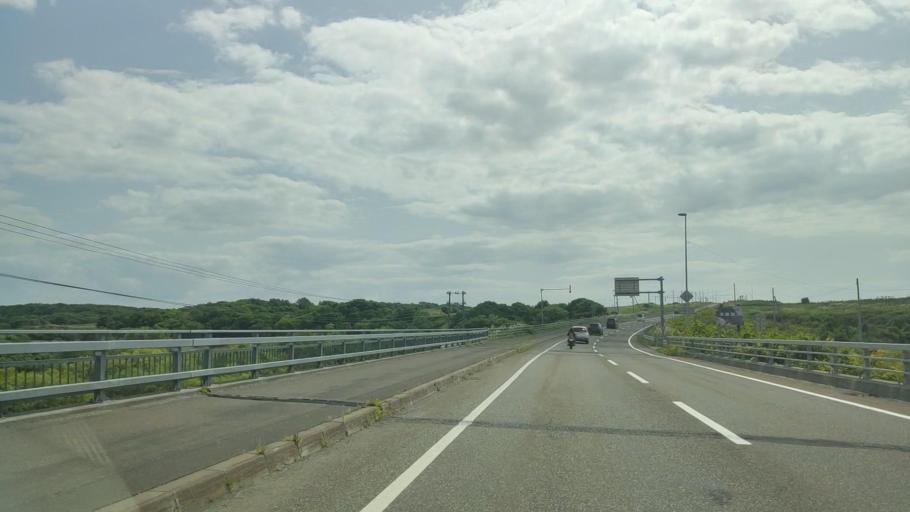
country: JP
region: Hokkaido
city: Rumoi
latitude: 44.4471
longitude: 141.7566
